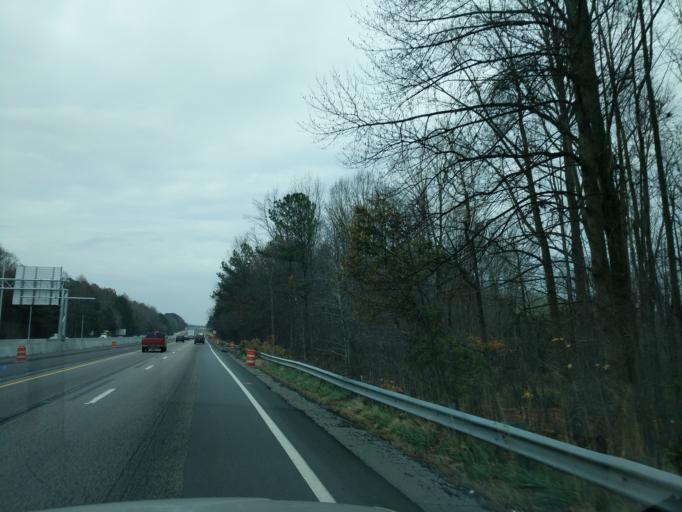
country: US
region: Georgia
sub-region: Gwinnett County
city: Buford
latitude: 34.0574
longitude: -83.9645
